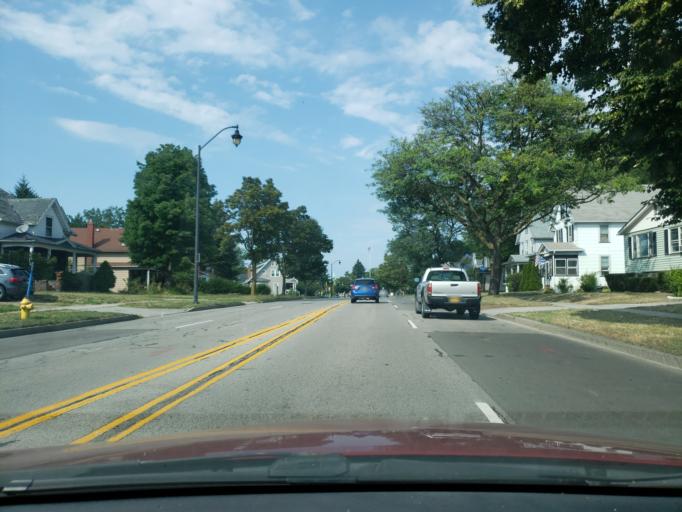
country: US
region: New York
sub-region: Monroe County
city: Irondequoit
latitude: 43.2423
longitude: -77.6197
